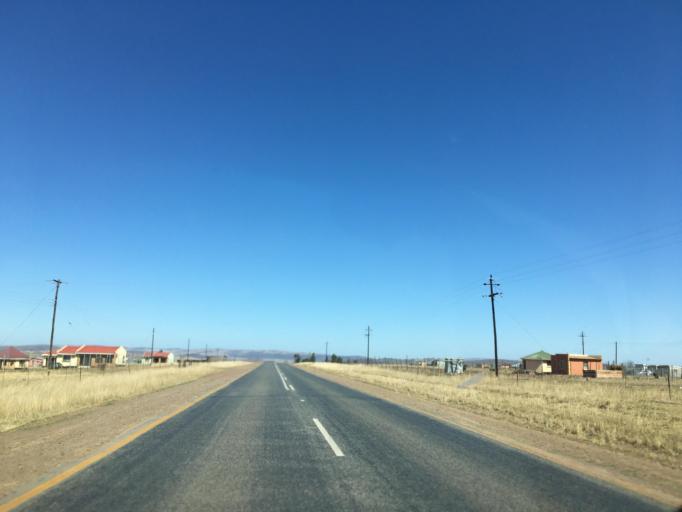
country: ZA
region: Eastern Cape
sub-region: Chris Hani District Municipality
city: Cofimvaba
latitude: -31.9300
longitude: 27.8372
